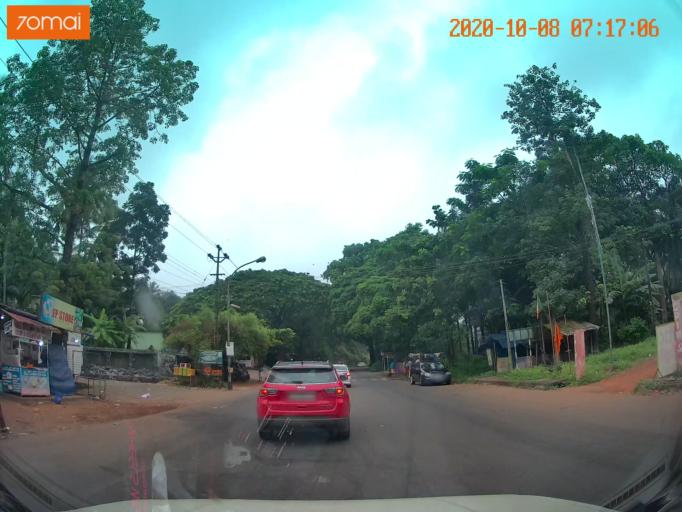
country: IN
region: Kerala
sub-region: Malappuram
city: Ponnani
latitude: 10.8357
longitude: 76.0175
